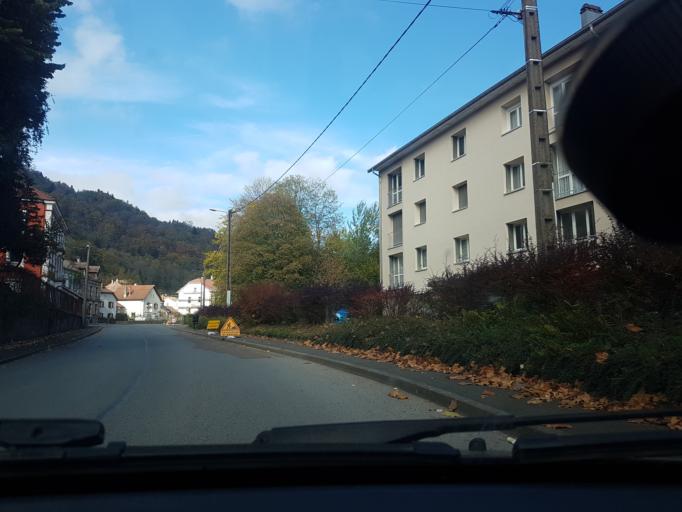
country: FR
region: Franche-Comte
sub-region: Departement de la Haute-Saone
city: Plancher-les-Mines
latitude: 47.7561
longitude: 6.7380
